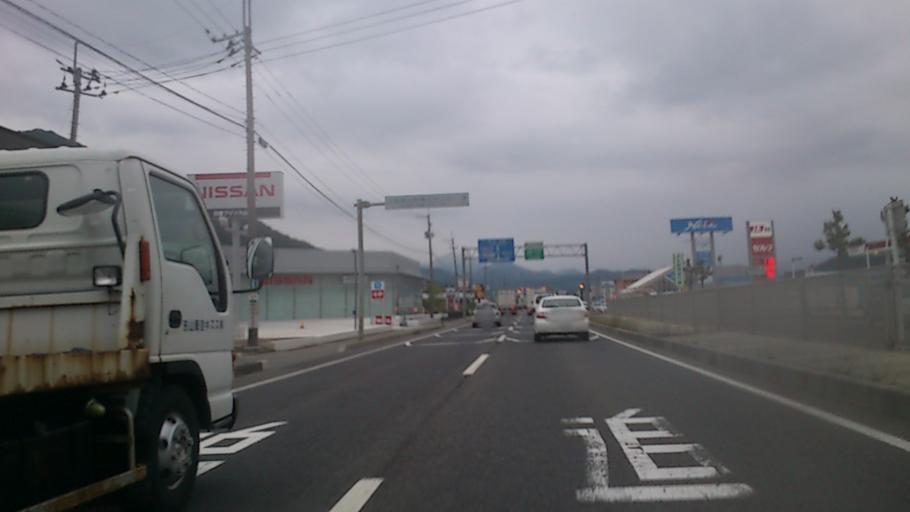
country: JP
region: Yamagata
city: Tendo
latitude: 38.3667
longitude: 140.3858
